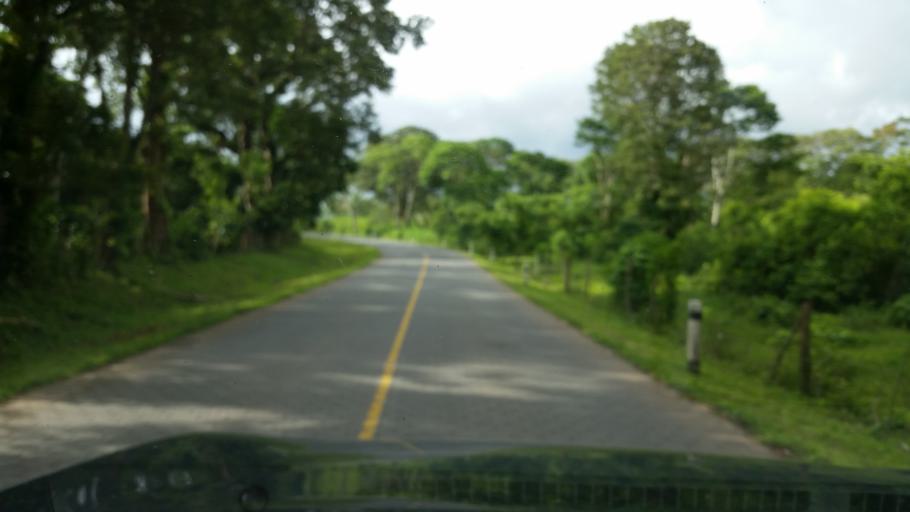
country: NI
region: Matagalpa
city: San Ramon
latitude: 13.1700
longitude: -85.7274
